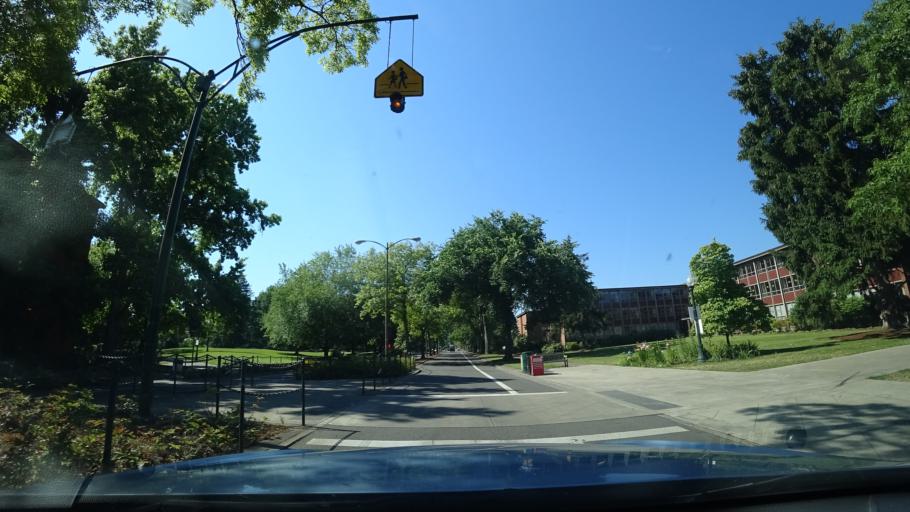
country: US
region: Oregon
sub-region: Lane County
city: Eugene
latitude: 44.0447
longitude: -123.0697
